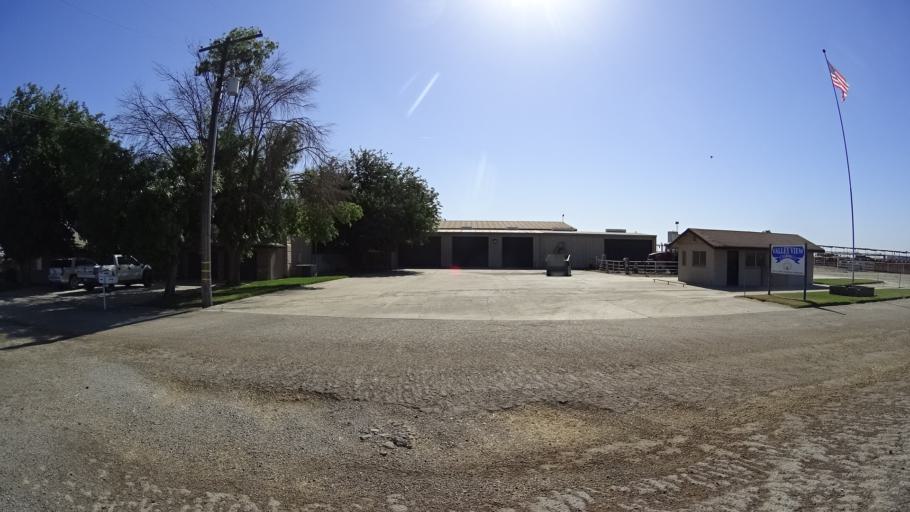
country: US
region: California
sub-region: Kings County
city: Home Garden
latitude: 36.2449
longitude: -119.5562
